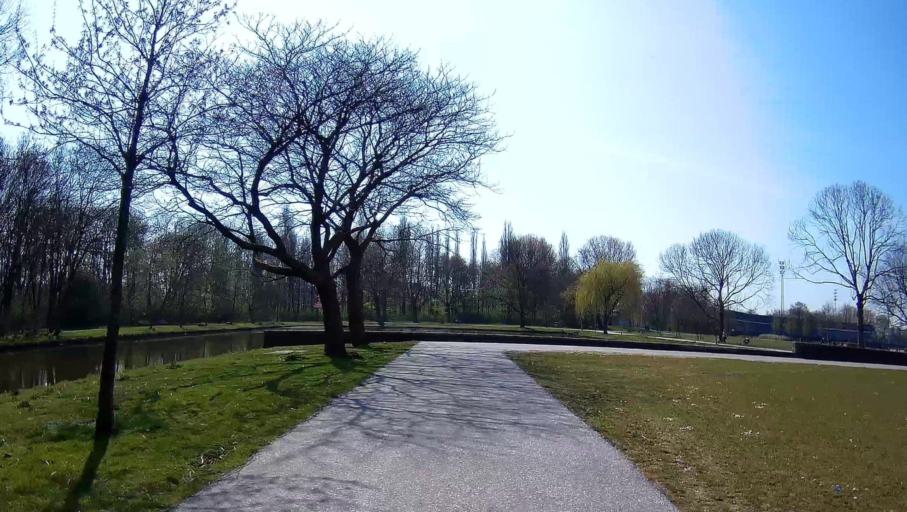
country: NL
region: South Holland
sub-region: Gemeente Rotterdam
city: Delfshaven
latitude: 51.9260
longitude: 4.4431
